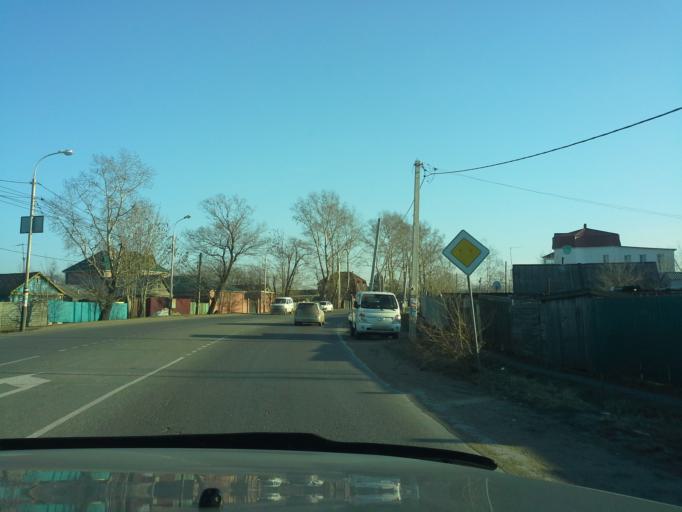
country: RU
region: Khabarovsk Krai
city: Topolevo
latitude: 48.4725
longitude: 135.1761
